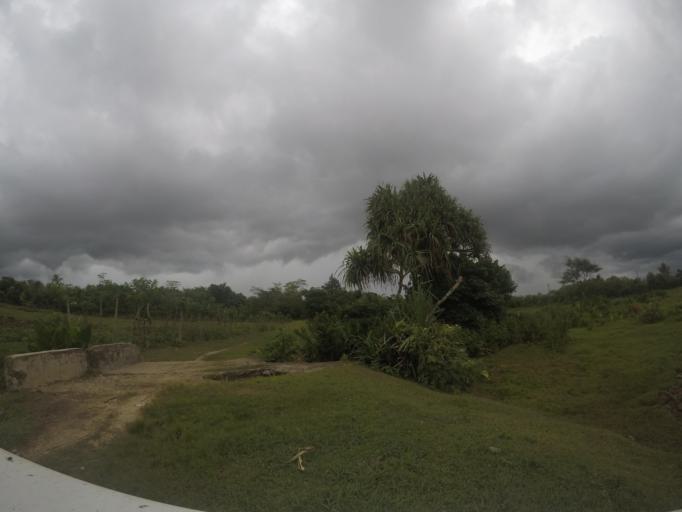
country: TL
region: Lautem
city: Lospalos
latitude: -8.5151
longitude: 126.9921
